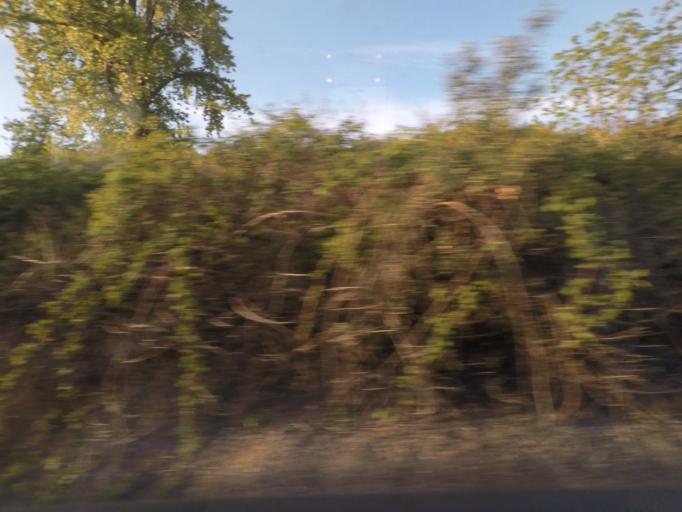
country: US
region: Washington
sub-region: Whatcom County
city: Bellingham
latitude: 48.7626
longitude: -122.5100
